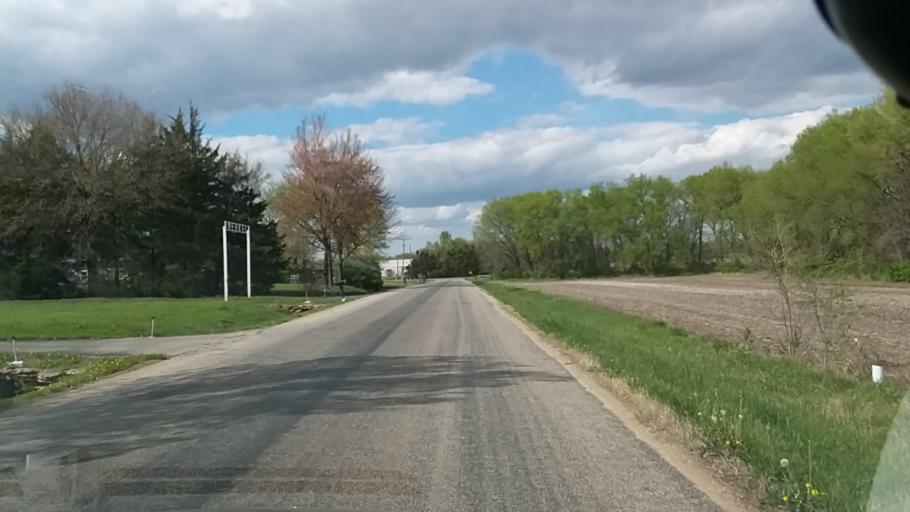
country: US
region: Kansas
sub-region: Douglas County
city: Lawrence
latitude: 38.8972
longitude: -95.2556
